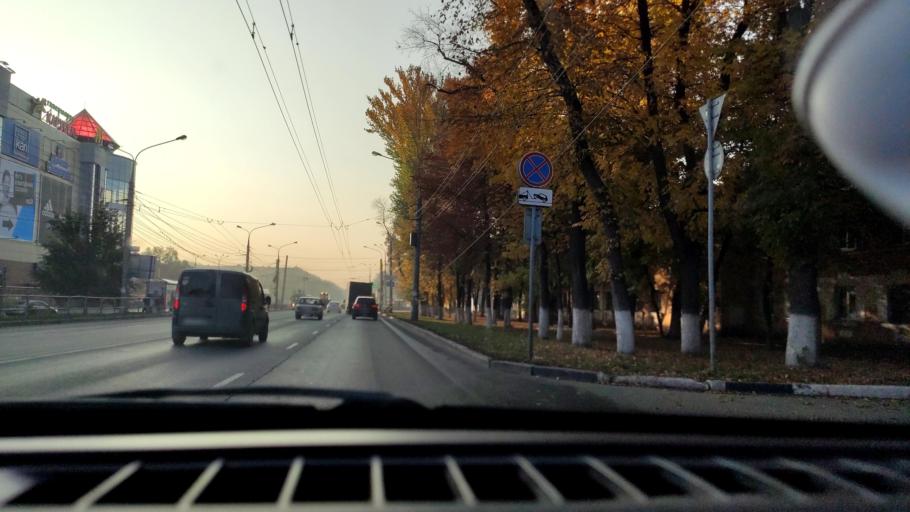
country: RU
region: Samara
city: Samara
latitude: 53.2206
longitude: 50.2610
